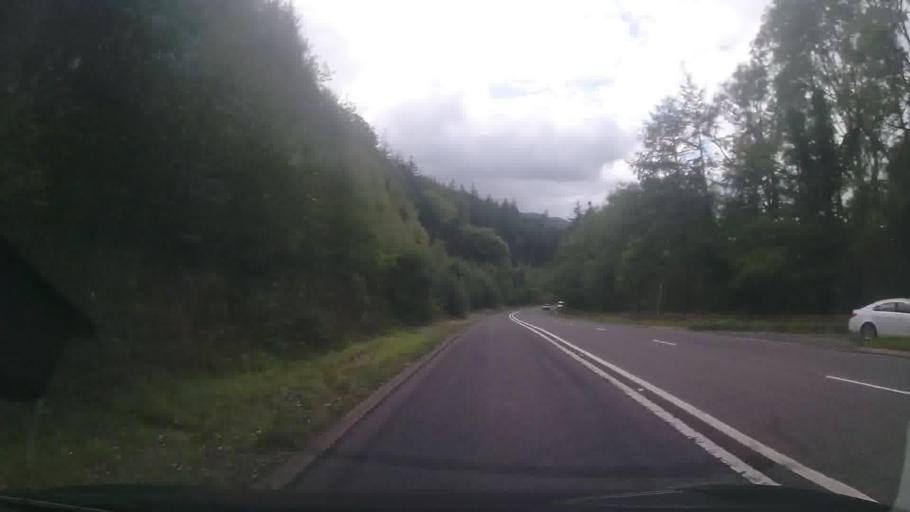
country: GB
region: Wales
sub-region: Gwynedd
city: Dolgellau
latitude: 52.7489
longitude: -3.8528
